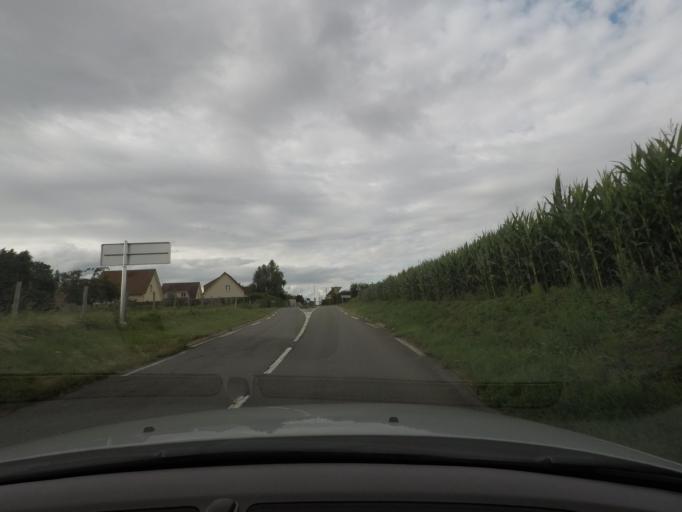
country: FR
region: Haute-Normandie
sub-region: Departement de la Seine-Maritime
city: Ymare
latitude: 49.3508
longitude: 1.1839
